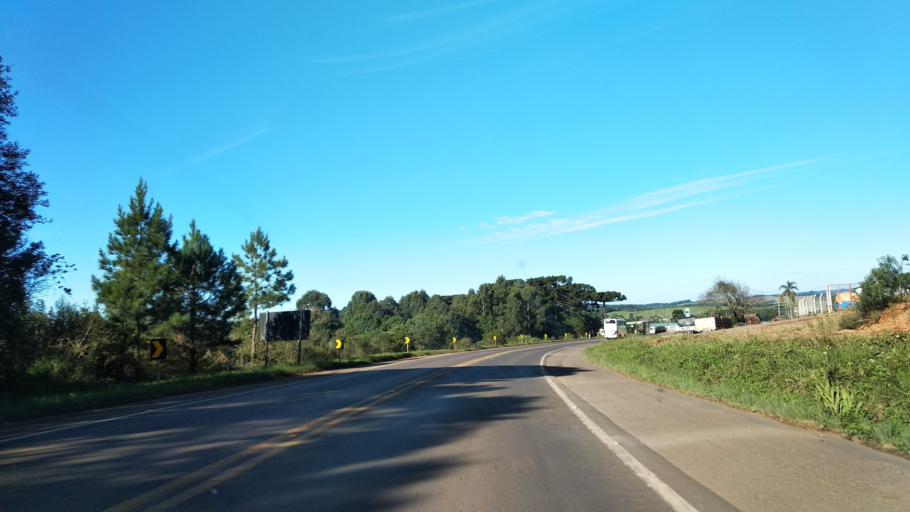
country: BR
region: Santa Catarina
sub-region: Campos Novos
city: Campos Novos
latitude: -27.3890
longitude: -51.2034
